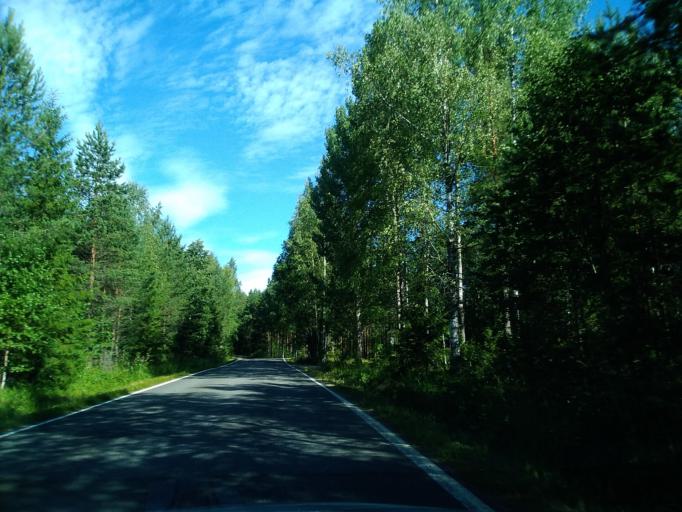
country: FI
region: Uusimaa
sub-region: Helsinki
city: Kaerkoelae
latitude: 60.7738
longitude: 24.0739
